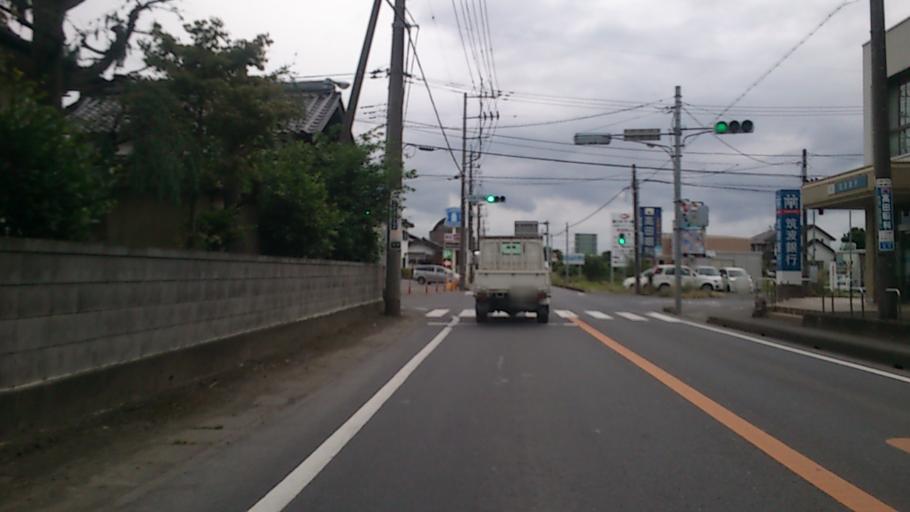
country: JP
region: Ibaraki
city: Ishige
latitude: 36.1052
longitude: 140.0486
